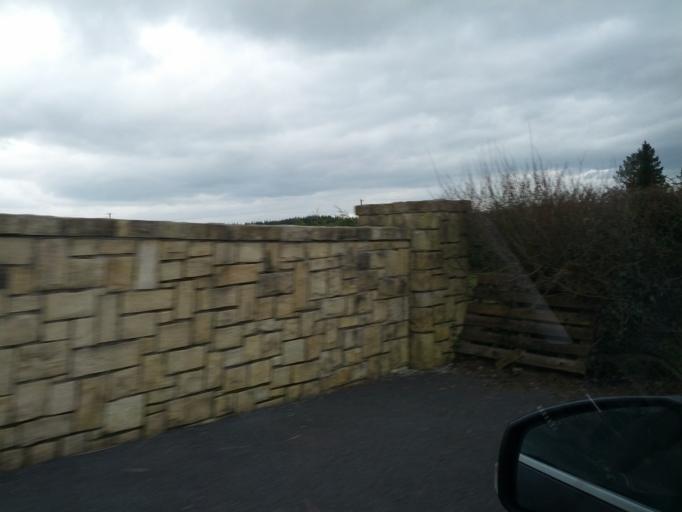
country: IE
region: Connaught
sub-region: County Galway
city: Athenry
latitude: 53.3895
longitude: -8.6424
